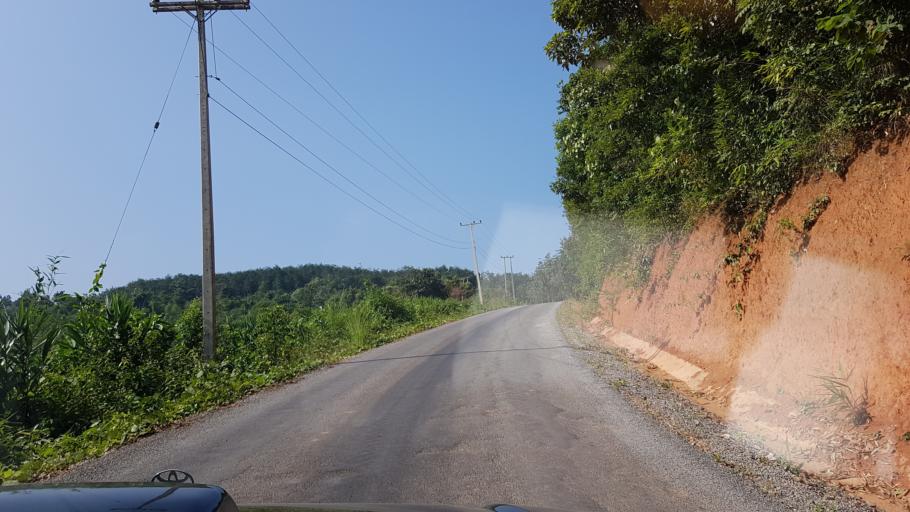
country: LA
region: Oudomxai
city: Muang Xay
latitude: 20.7122
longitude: 102.0847
